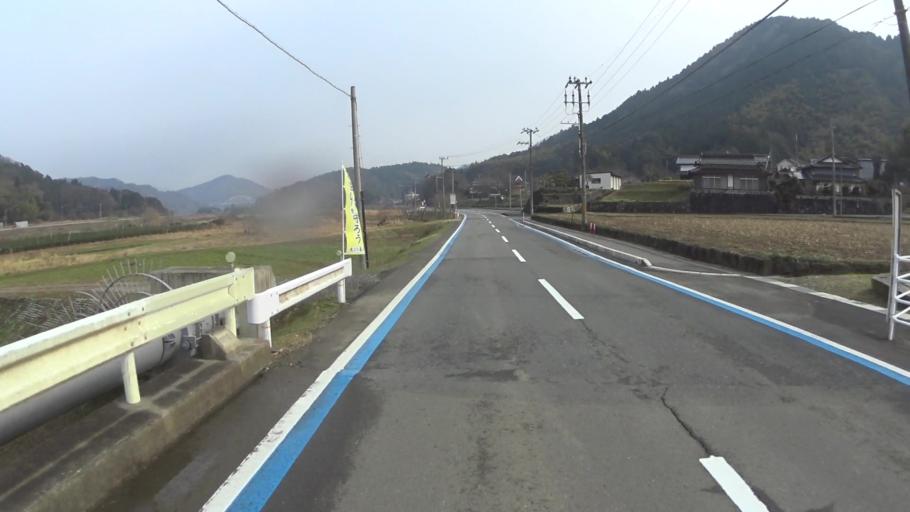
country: JP
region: Kyoto
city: Ayabe
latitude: 35.4088
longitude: 135.1968
